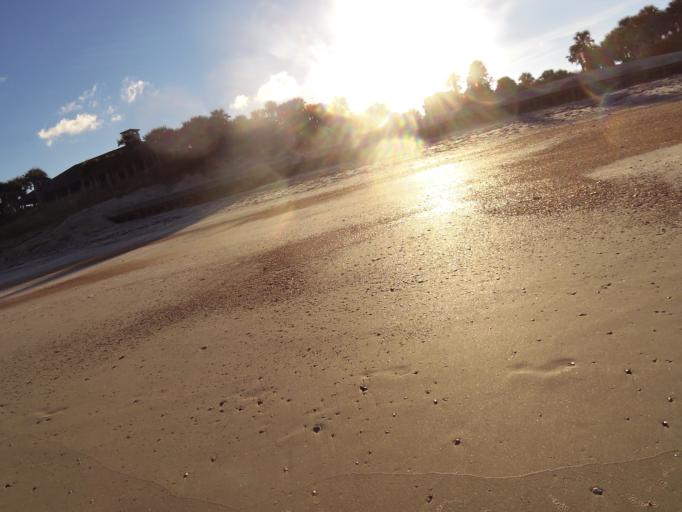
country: US
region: Florida
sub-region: Saint Johns County
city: Sawgrass
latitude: 30.1779
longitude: -81.3597
